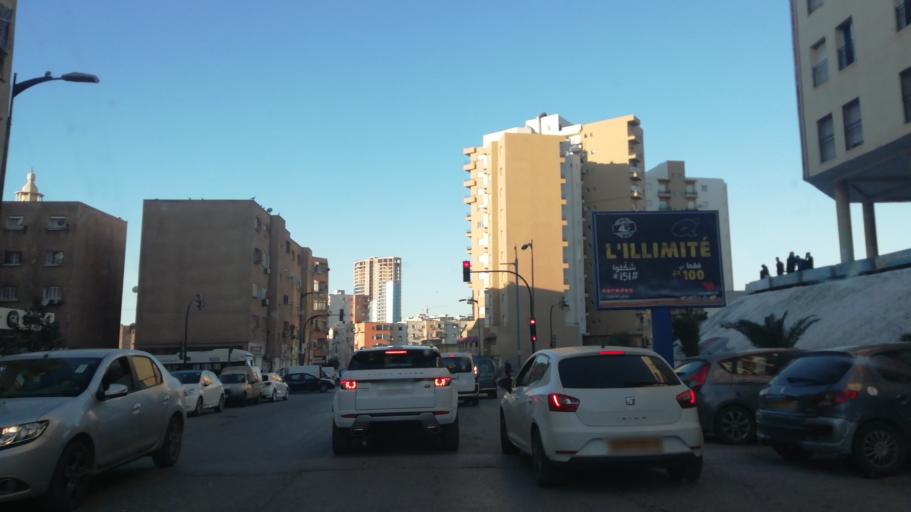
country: DZ
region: Oran
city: Bir el Djir
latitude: 35.7223
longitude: -0.5877
